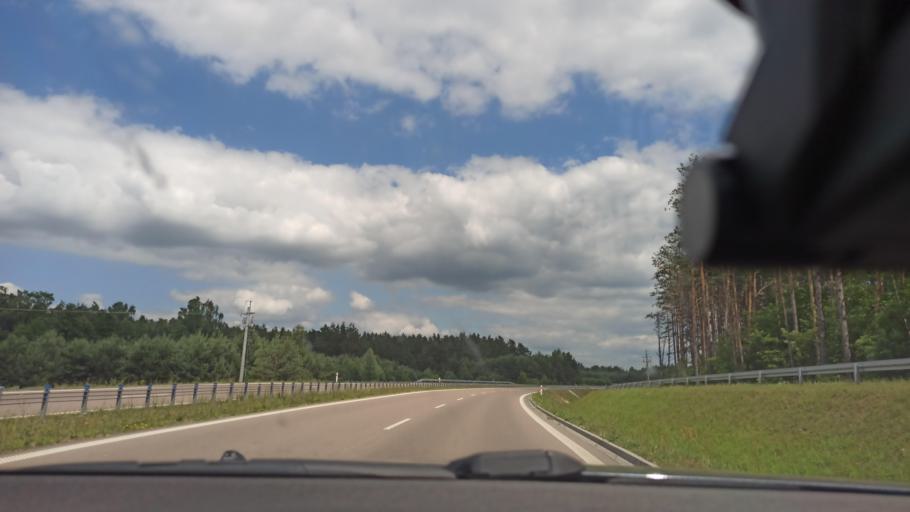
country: PL
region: Podlasie
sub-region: Powiat bialostocki
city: Suraz
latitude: 53.0168
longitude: 22.9781
